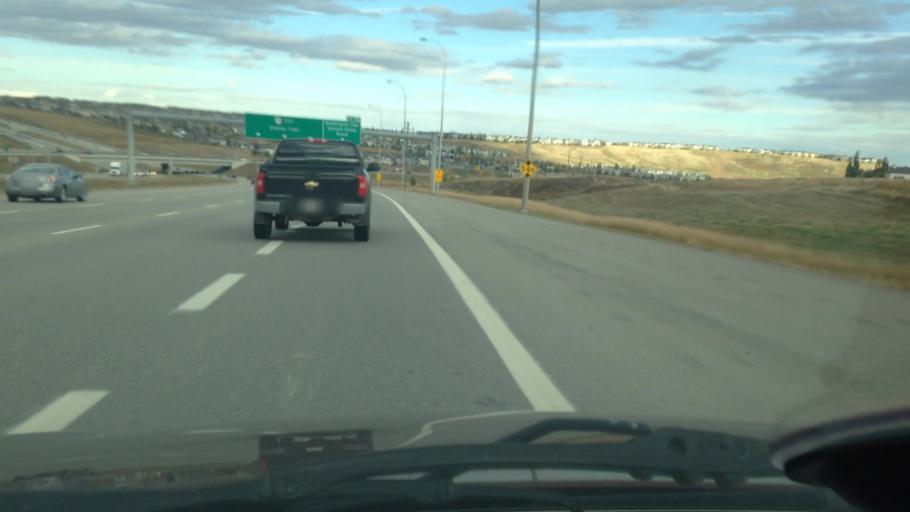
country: CA
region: Alberta
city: Calgary
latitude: 51.1536
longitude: -114.1237
